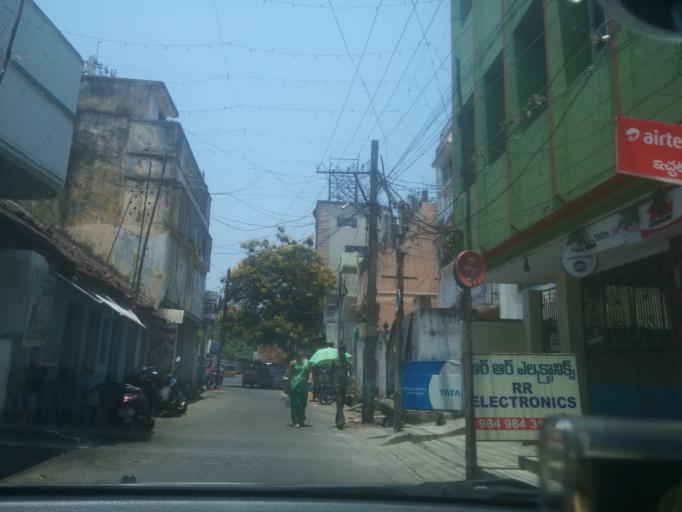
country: IN
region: Andhra Pradesh
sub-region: East Godavari
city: Rajahmundry
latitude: 16.9963
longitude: 81.7757
